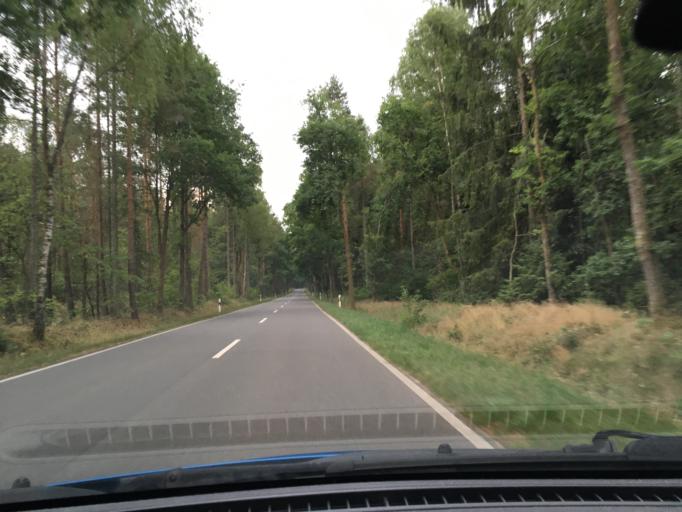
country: DE
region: Lower Saxony
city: Unterluss
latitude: 52.7766
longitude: 10.3038
